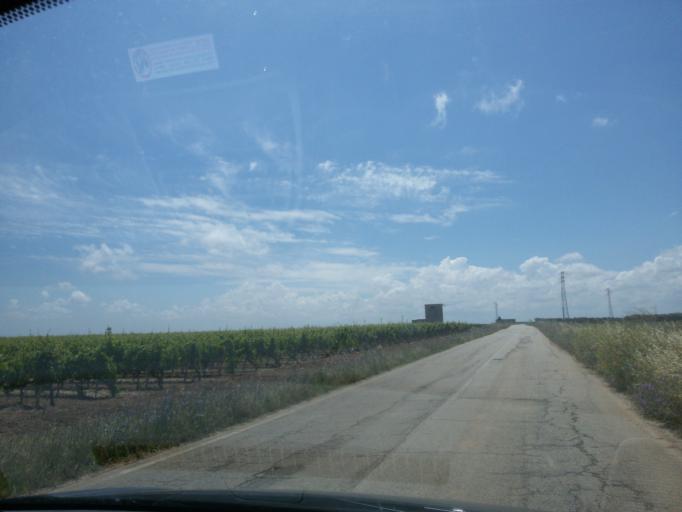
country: IT
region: Apulia
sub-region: Provincia di Brindisi
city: Brindisi
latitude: 40.6693
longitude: 17.8422
